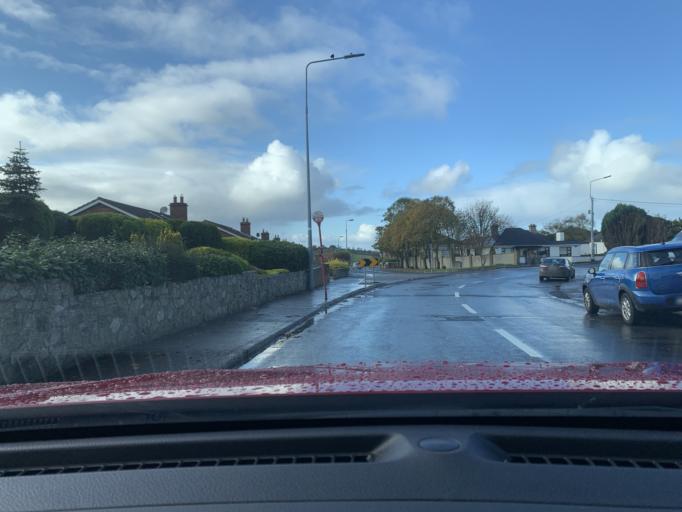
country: IE
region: Connaught
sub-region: Sligo
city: Sligo
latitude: 54.2607
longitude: -8.4695
